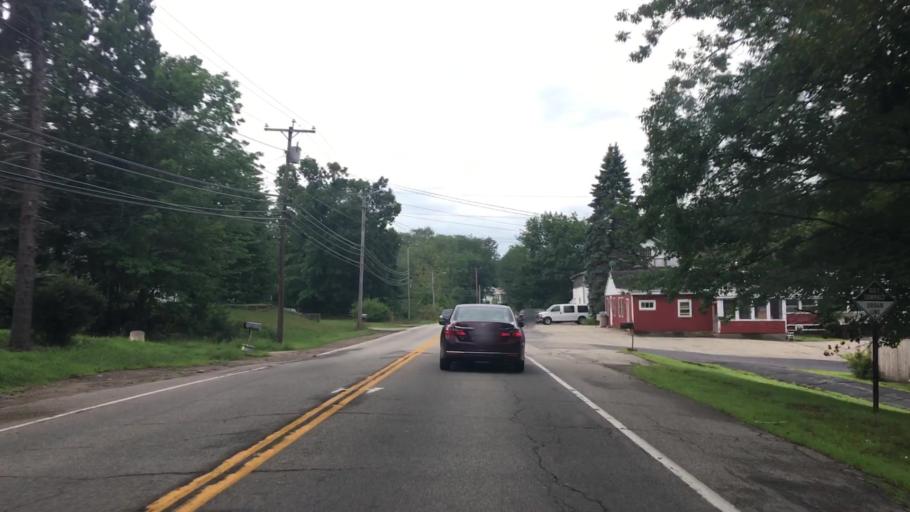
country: US
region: Maine
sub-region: York County
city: Sanford (historical)
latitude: 43.4524
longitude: -70.7667
